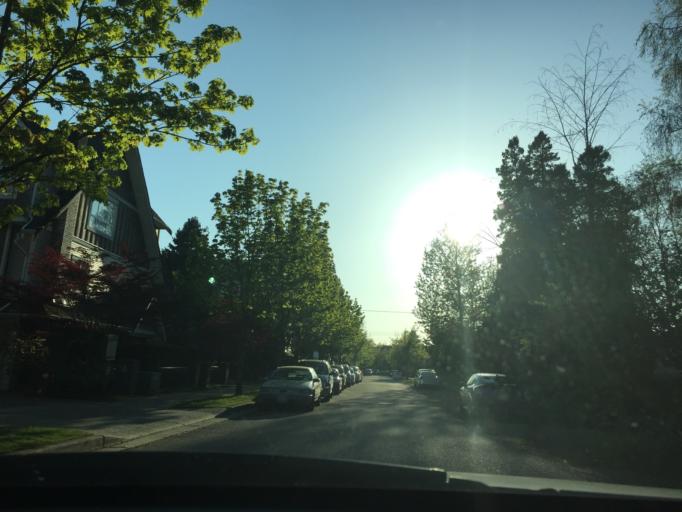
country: CA
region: British Columbia
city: Richmond
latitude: 49.1565
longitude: -123.1212
